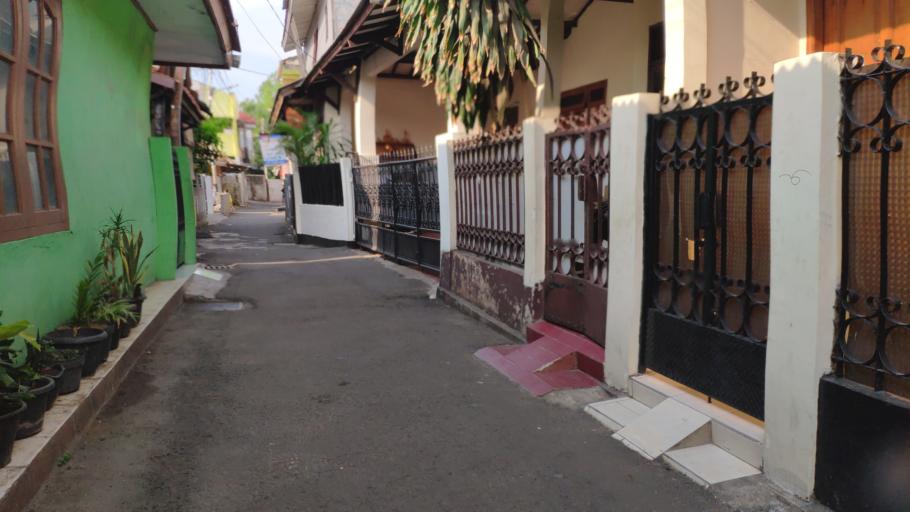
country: ID
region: West Java
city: Pamulang
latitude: -6.3096
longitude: 106.7986
